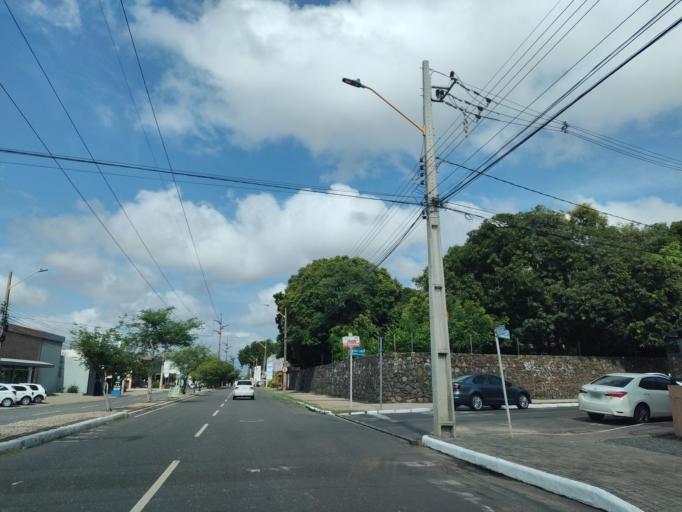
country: BR
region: Piaui
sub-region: Teresina
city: Teresina
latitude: -5.0700
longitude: -42.7857
